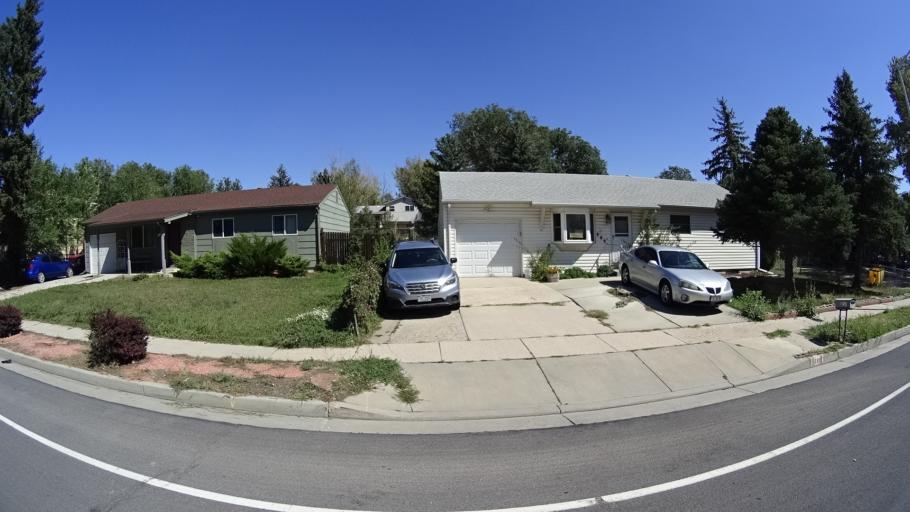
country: US
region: Colorado
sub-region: El Paso County
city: Cimarron Hills
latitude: 38.8272
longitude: -104.7486
